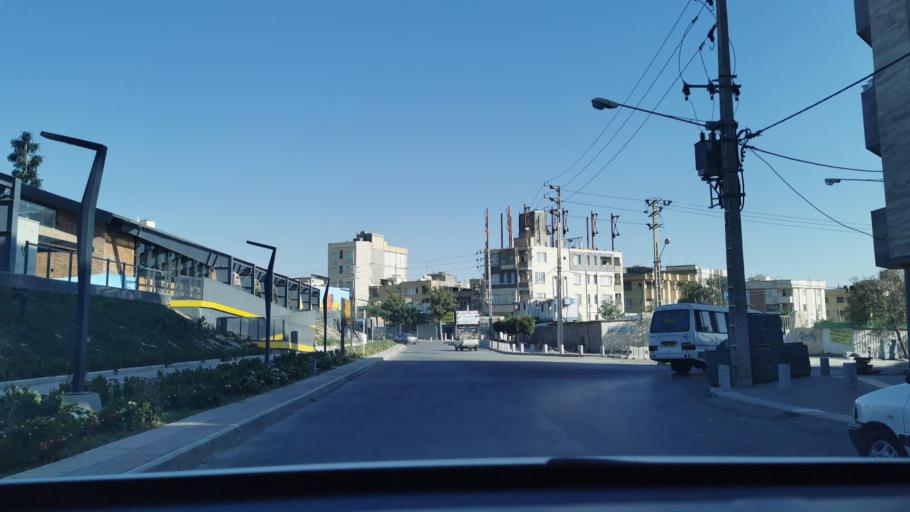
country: IR
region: Razavi Khorasan
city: Mashhad
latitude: 36.3112
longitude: 59.5133
